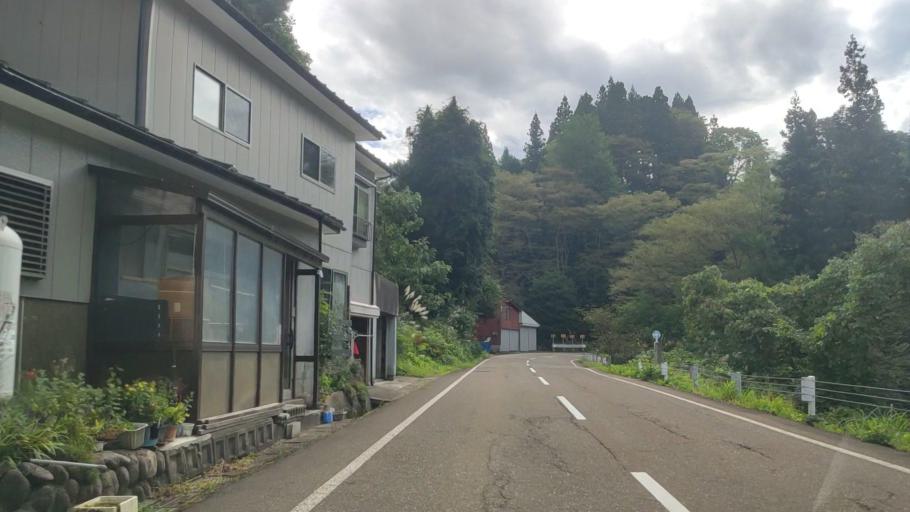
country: JP
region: Niigata
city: Arai
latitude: 36.9314
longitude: 138.2982
